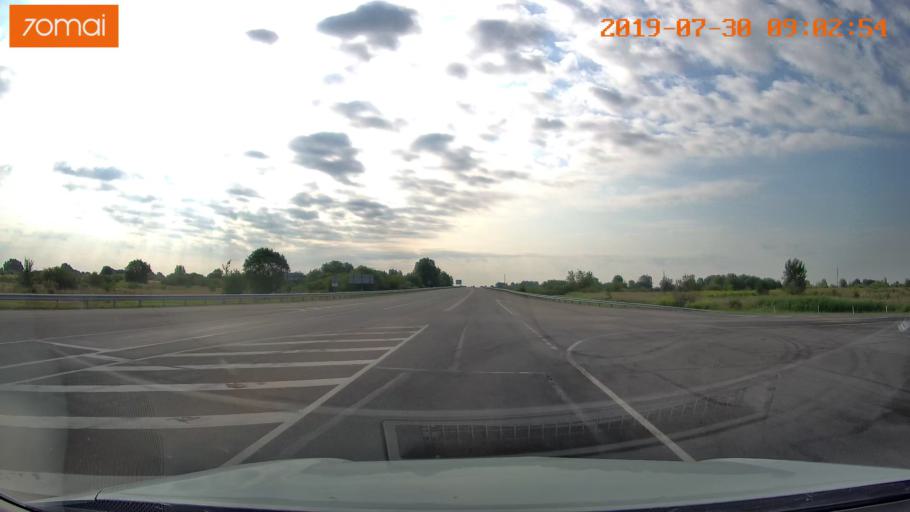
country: RU
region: Kaliningrad
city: Gusev
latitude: 54.6123
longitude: 22.2416
